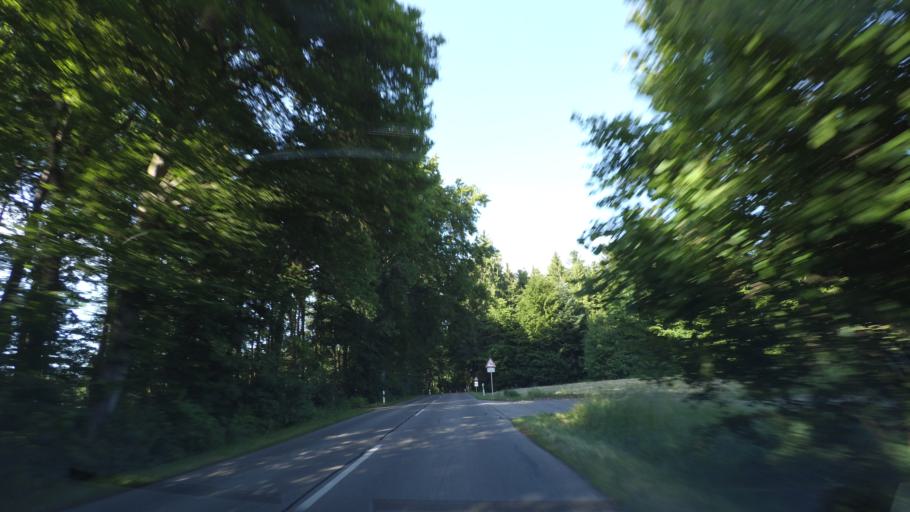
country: DE
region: Baden-Wuerttemberg
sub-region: Regierungsbezirk Stuttgart
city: Welzheim
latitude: 48.8952
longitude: 9.6592
